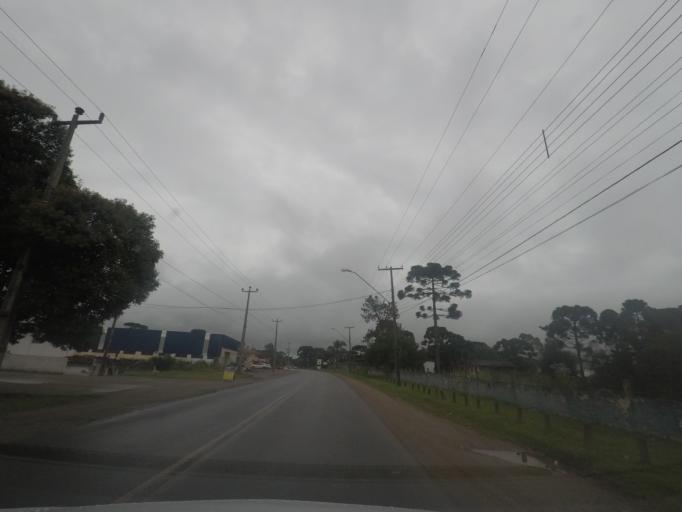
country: BR
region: Parana
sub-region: Quatro Barras
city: Quatro Barras
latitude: -25.3350
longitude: -49.0795
